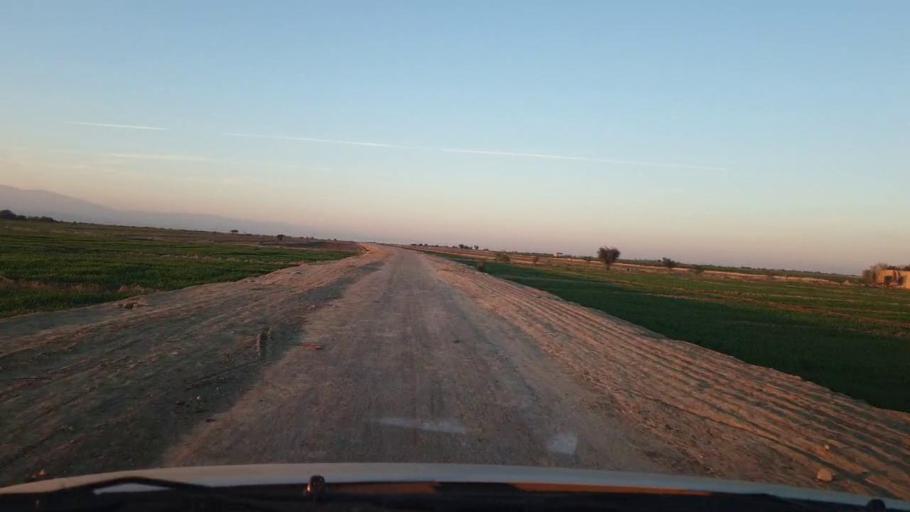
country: PK
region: Sindh
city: Johi
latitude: 26.8349
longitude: 67.4420
